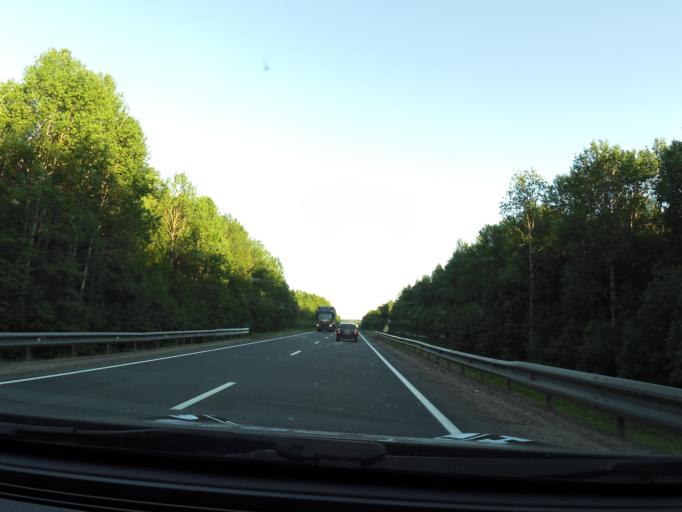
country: RU
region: Vologda
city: Gryazovets
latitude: 58.7589
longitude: 40.2814
